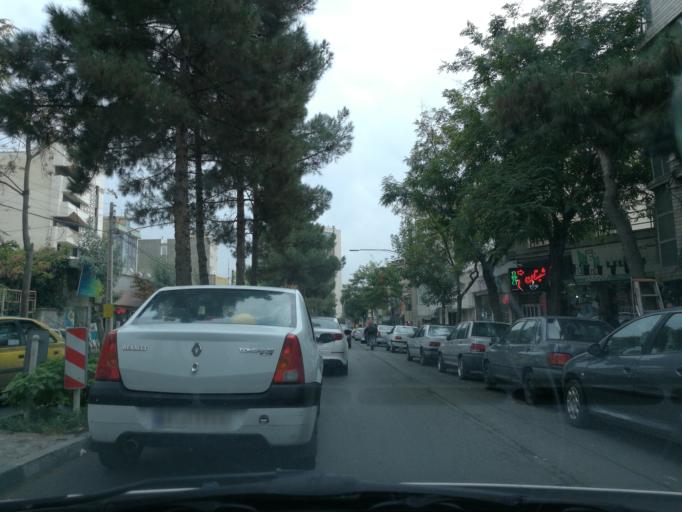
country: IR
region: Alborz
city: Karaj
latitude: 35.8464
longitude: 50.9697
